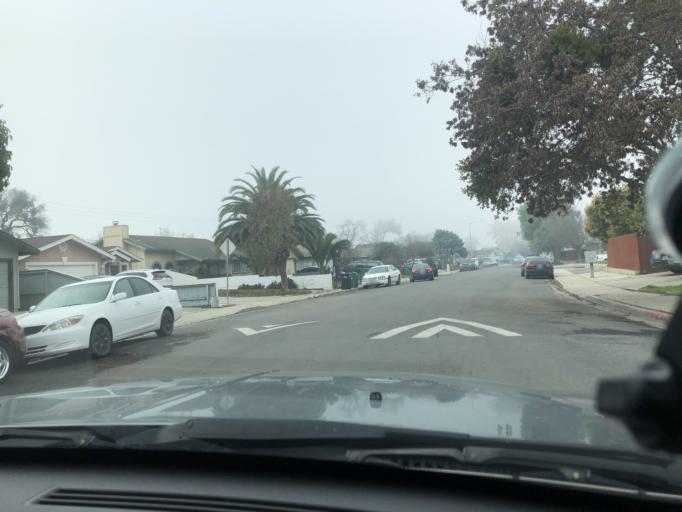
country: US
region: California
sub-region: Monterey County
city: King City
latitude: 36.2043
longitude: -121.1415
